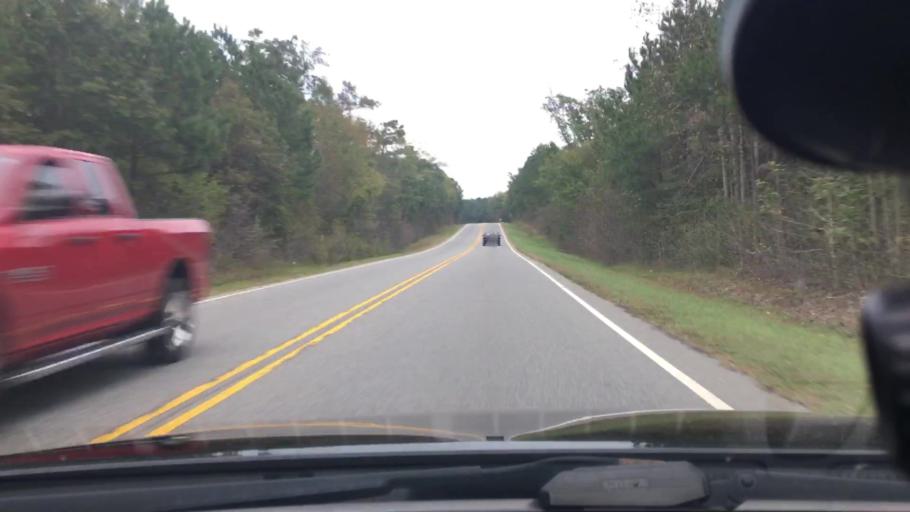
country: US
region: North Carolina
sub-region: Montgomery County
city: Biscoe
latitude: 35.3638
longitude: -79.6861
